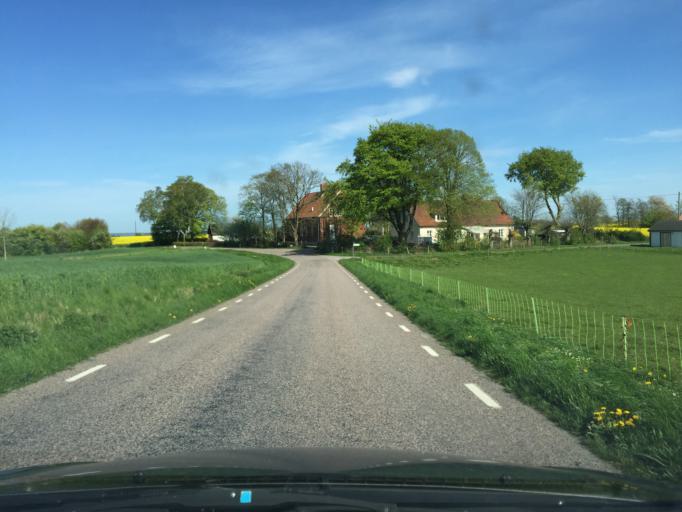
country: SE
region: Skane
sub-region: Sjobo Kommun
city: Blentarp
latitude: 55.5682
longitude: 13.5533
